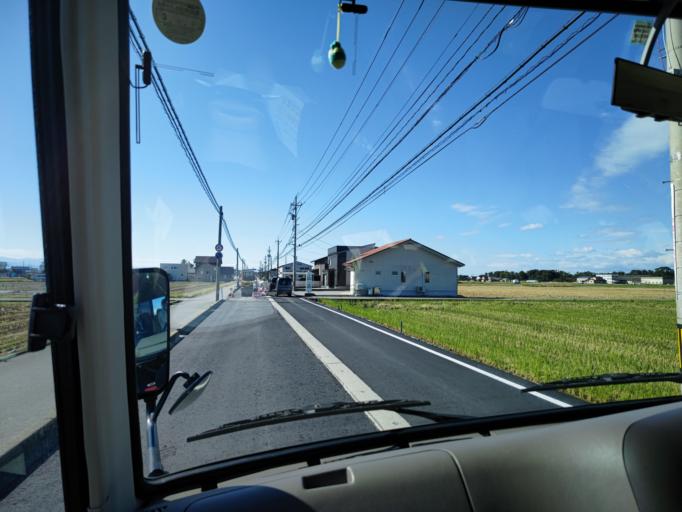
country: JP
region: Toyama
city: Nyuzen
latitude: 36.9015
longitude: 137.4225
